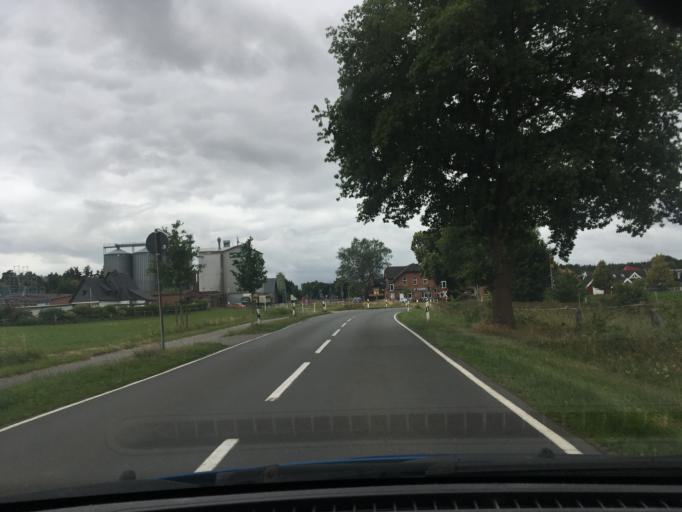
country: DE
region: Lower Saxony
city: Wulfsen
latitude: 53.2944
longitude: 10.1475
